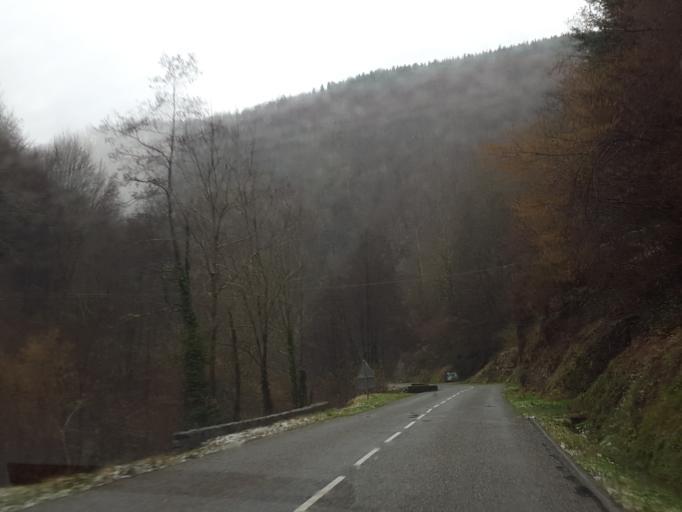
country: FR
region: Midi-Pyrenees
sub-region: Departement de l'Ariege
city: Saint-Girons
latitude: 42.9068
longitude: 1.2924
